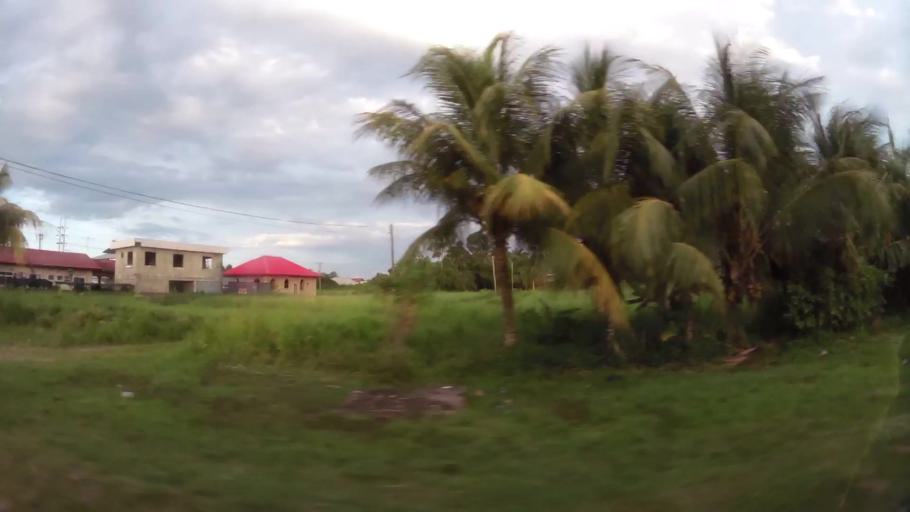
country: SR
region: Paramaribo
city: Paramaribo
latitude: 5.7801
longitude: -55.1672
